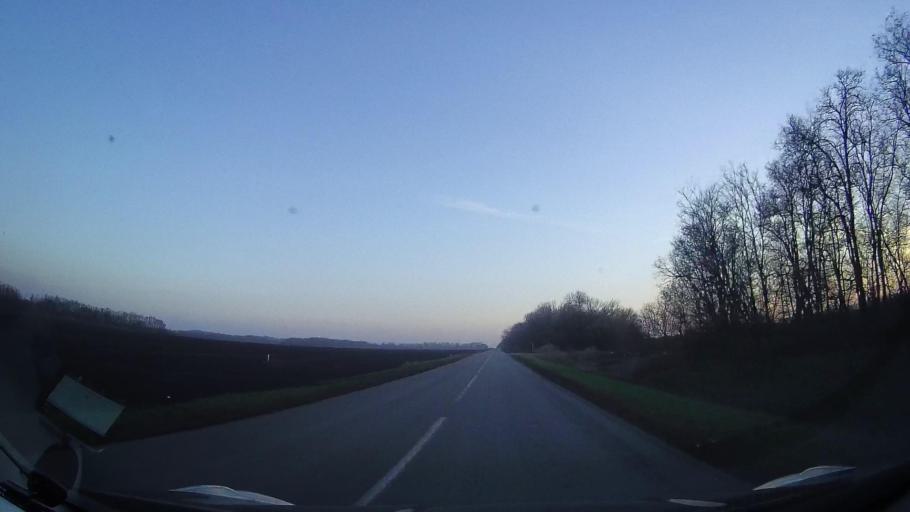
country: RU
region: Rostov
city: Zernograd
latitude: 47.0024
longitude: 40.3915
